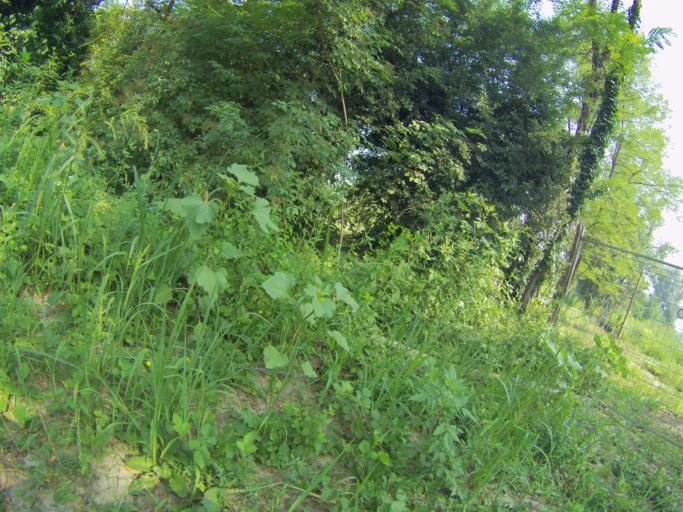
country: IT
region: Emilia-Romagna
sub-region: Provincia di Reggio Emilia
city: Pratissolo
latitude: 44.5931
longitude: 10.6750
